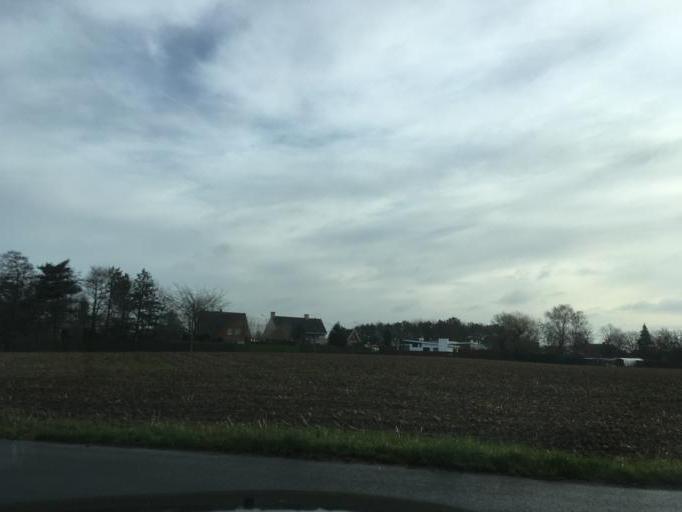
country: BE
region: Flanders
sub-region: Provincie West-Vlaanderen
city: Hooglede
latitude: 50.9628
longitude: 3.0945
